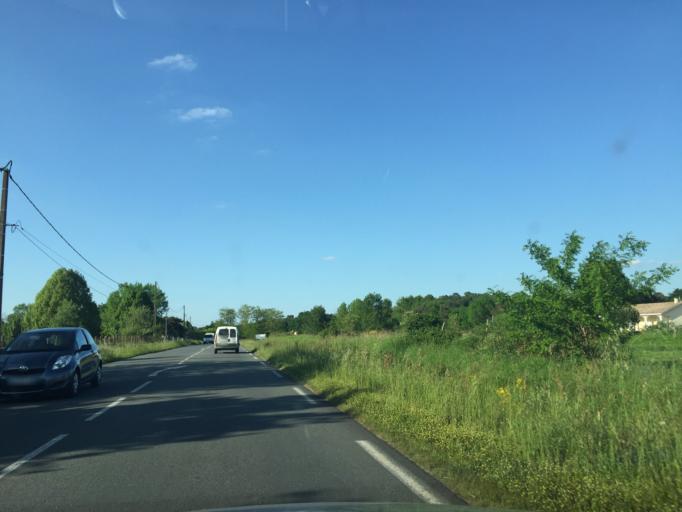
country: FR
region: Poitou-Charentes
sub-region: Departement de la Charente-Maritime
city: Saint-Aigulin
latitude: 45.1339
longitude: -0.0045
